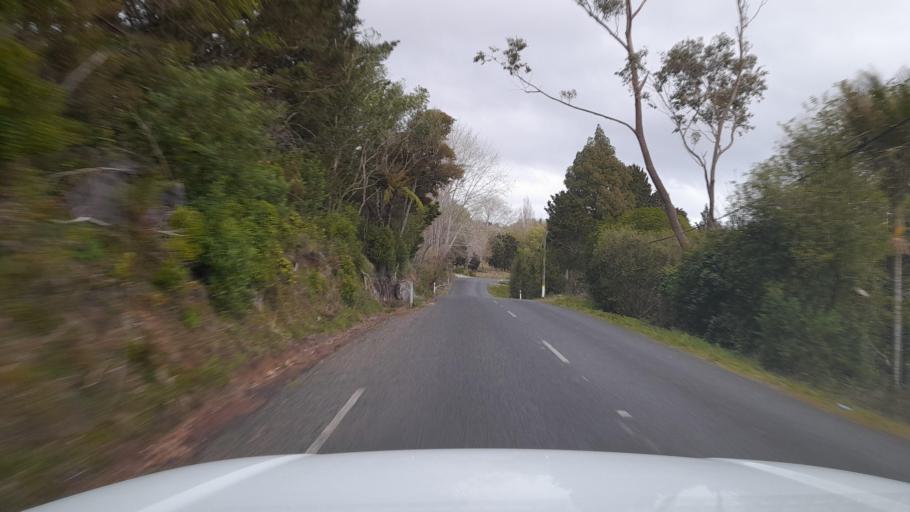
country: NZ
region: Northland
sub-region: Whangarei
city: Maungatapere
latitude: -35.6387
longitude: 174.2105
